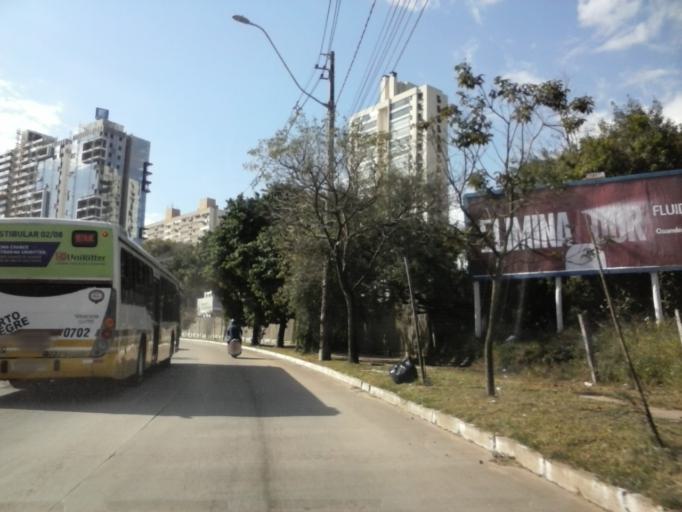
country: BR
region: Rio Grande do Sul
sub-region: Porto Alegre
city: Porto Alegre
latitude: -30.0428
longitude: -51.1737
